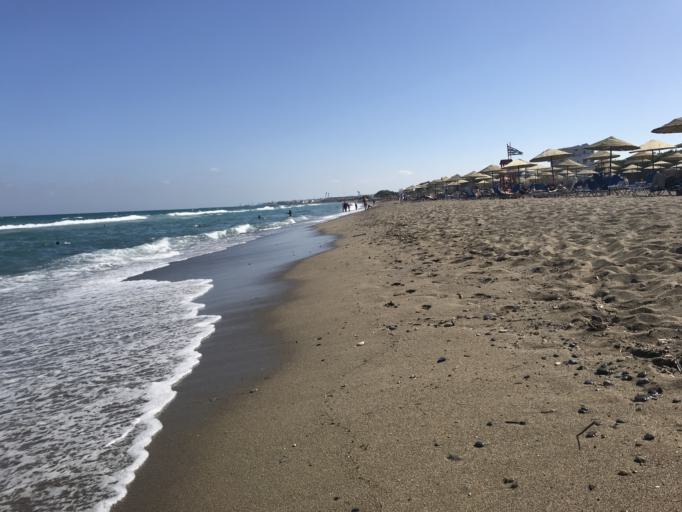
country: GR
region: Crete
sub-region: Nomos Irakleiou
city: Gazi
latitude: 35.3383
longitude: 25.0723
